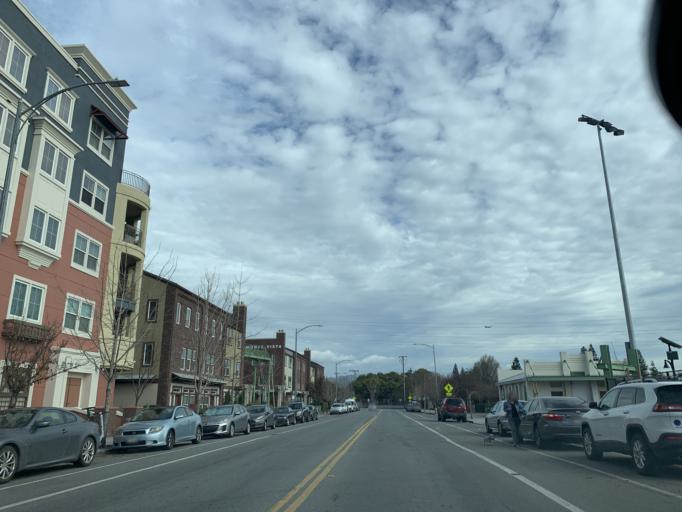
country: US
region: California
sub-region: Santa Clara County
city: Buena Vista
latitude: 37.3212
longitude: -121.9047
